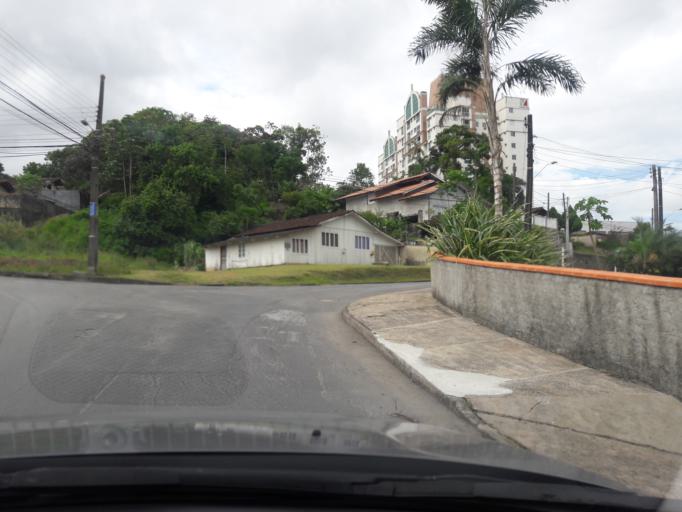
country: BR
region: Santa Catarina
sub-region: Joinville
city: Joinville
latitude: -26.3217
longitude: -48.8653
